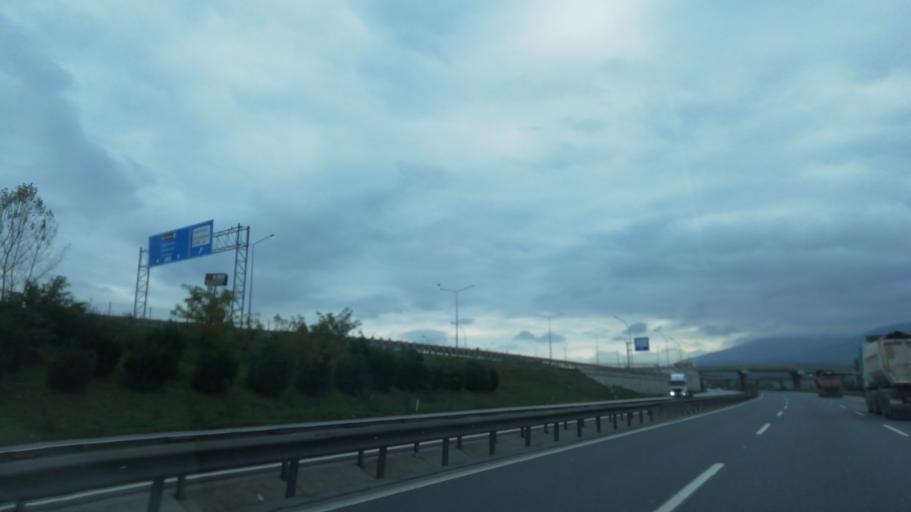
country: TR
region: Kocaeli
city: Kosekoy
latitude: 40.7336
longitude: 30.0537
